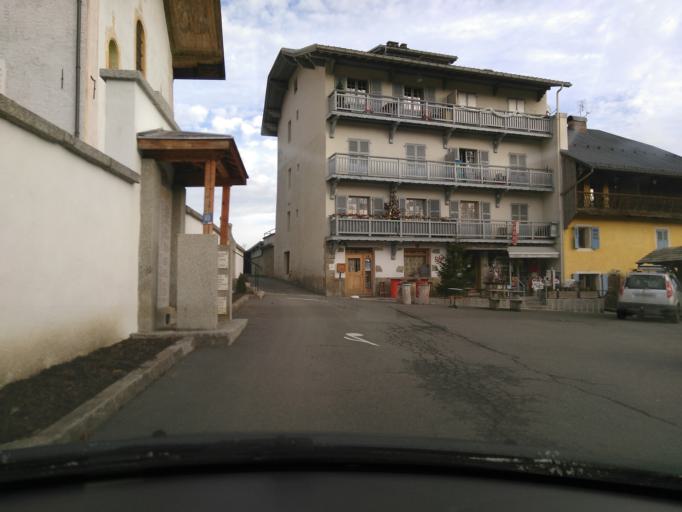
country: FR
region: Rhone-Alpes
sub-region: Departement de la Haute-Savoie
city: Cordon
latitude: 45.9222
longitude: 6.6104
